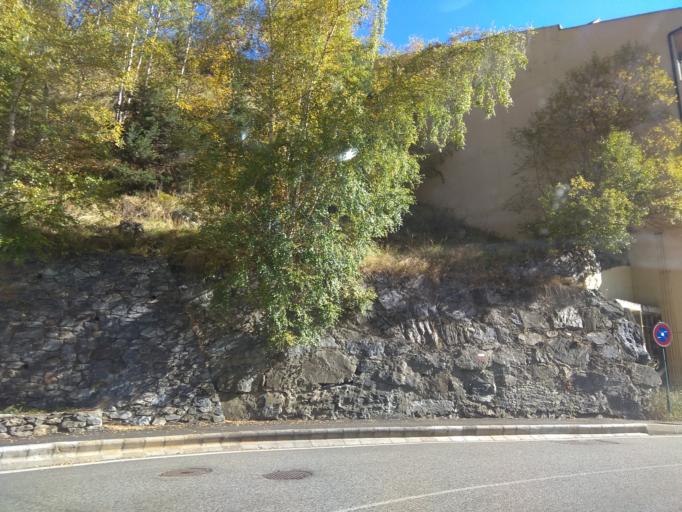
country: AD
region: La Massana
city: Arinsal
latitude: 42.5783
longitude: 1.4789
